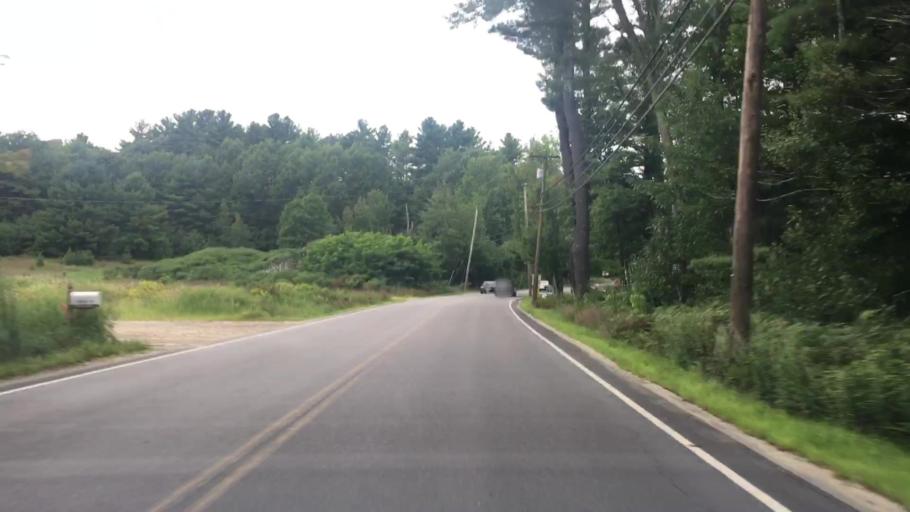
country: US
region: Maine
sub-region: York County
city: Dayton
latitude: 43.5129
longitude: -70.5857
